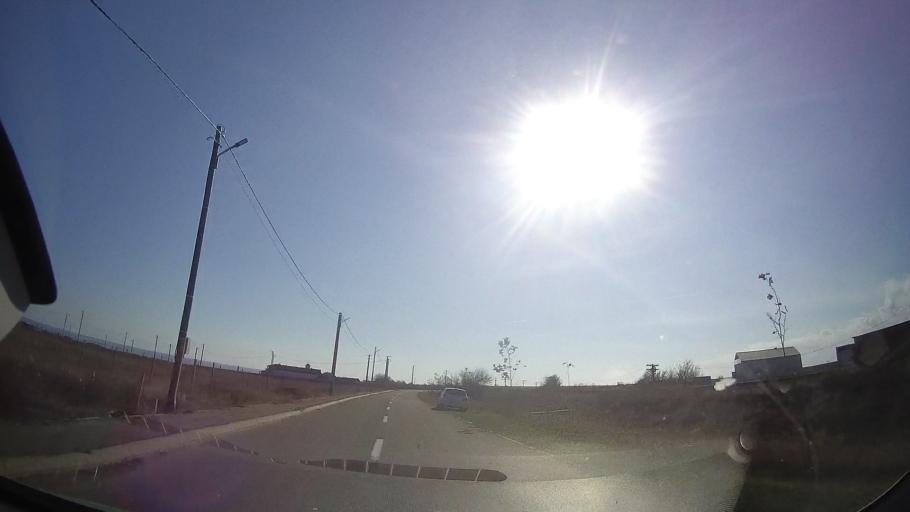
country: RO
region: Constanta
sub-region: Comuna Costinesti
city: Schitu
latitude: 43.9269
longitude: 28.6325
